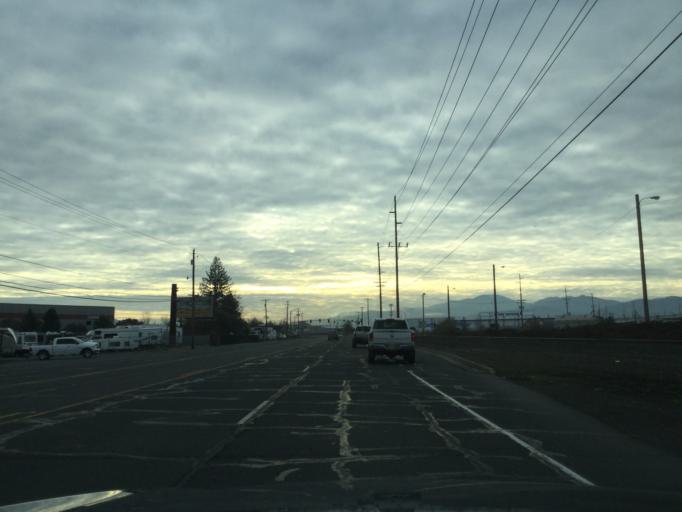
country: US
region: Oregon
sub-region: Jackson County
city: Central Point
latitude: 42.3548
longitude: -122.9006
